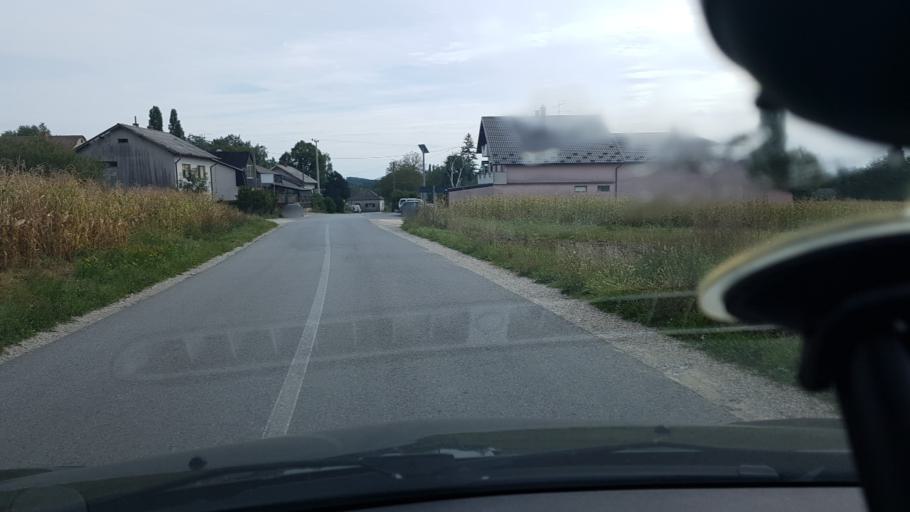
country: HR
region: Varazdinska
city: Ljubescica
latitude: 46.1084
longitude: 16.4191
